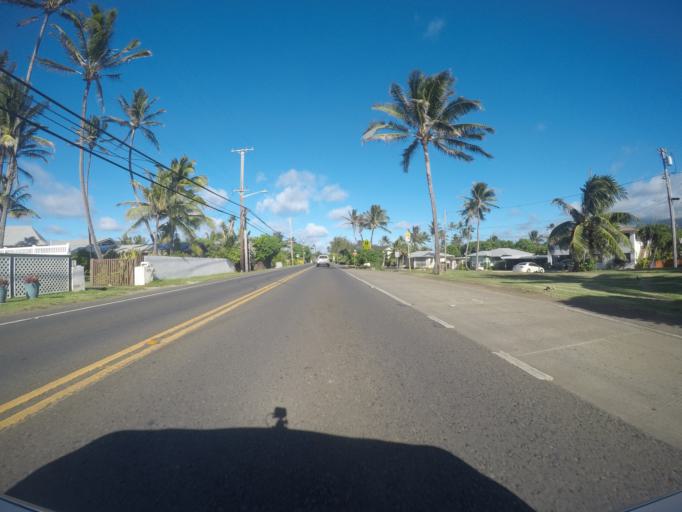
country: US
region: Hawaii
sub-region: Honolulu County
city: La'ie
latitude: 21.6514
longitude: -157.9271
